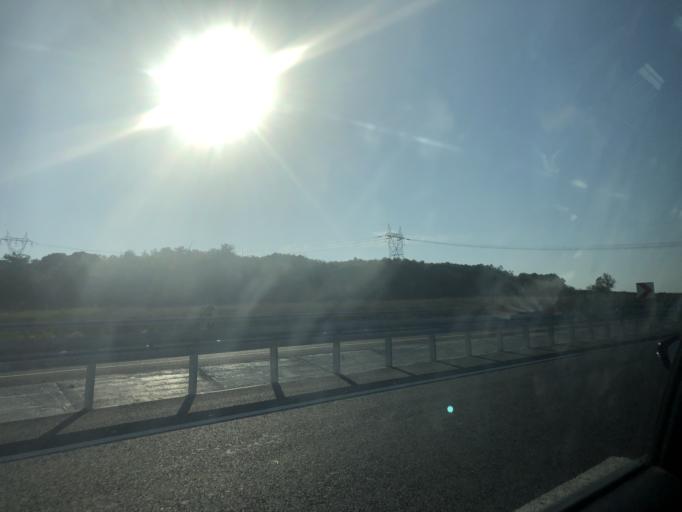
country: TR
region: Istanbul
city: Catalca
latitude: 41.1531
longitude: 28.4677
